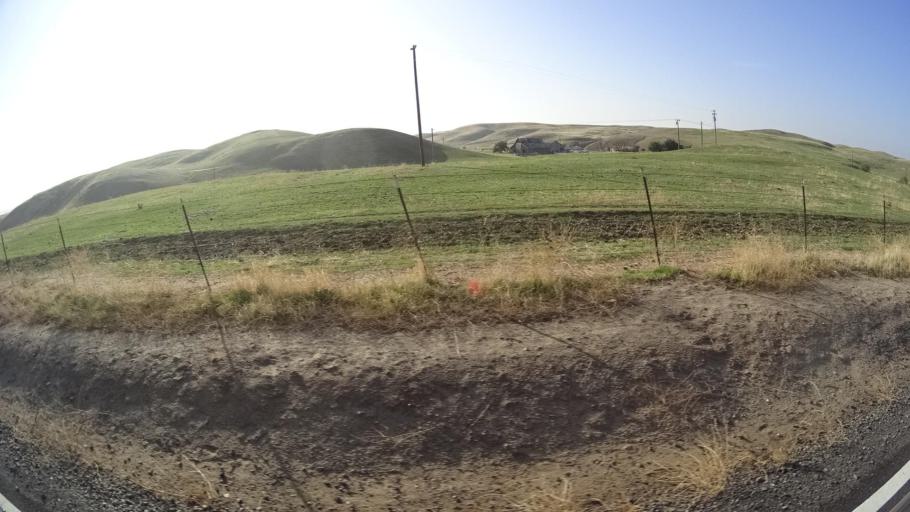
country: US
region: California
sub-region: Tulare County
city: Richgrove
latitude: 35.7398
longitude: -118.9563
